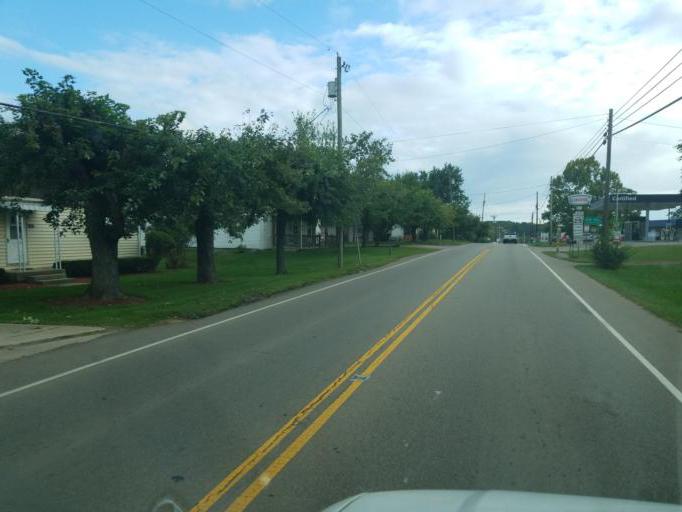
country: US
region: Ohio
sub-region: Jackson County
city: Oak Hill
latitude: 38.9030
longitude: -82.5689
